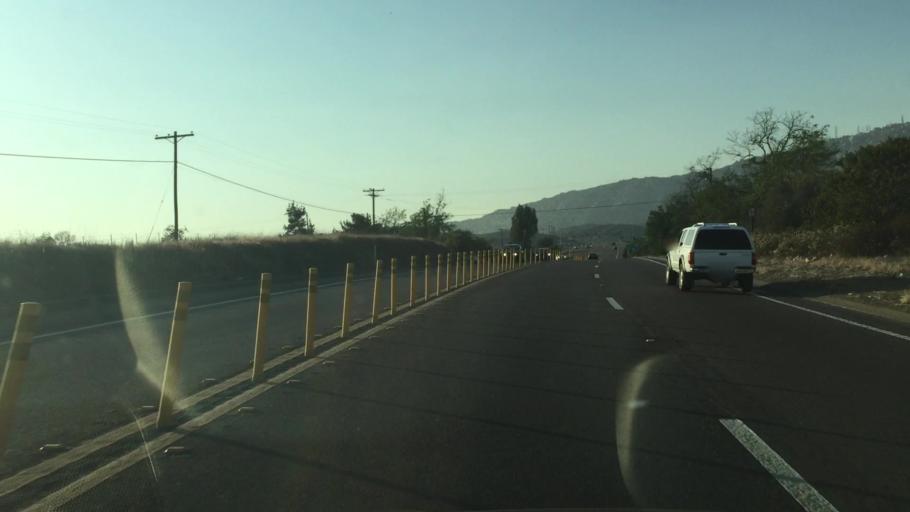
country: US
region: California
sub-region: San Diego County
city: Poway
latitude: 32.9733
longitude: -116.9717
